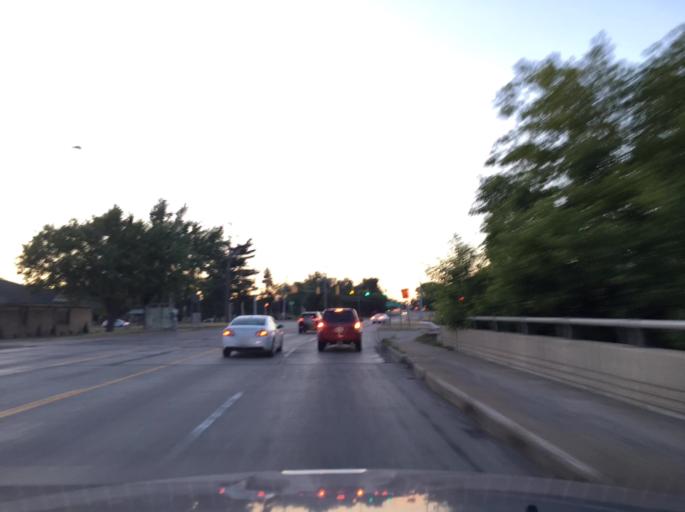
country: US
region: Michigan
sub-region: Macomb County
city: Clinton
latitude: 42.5781
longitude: -82.9520
